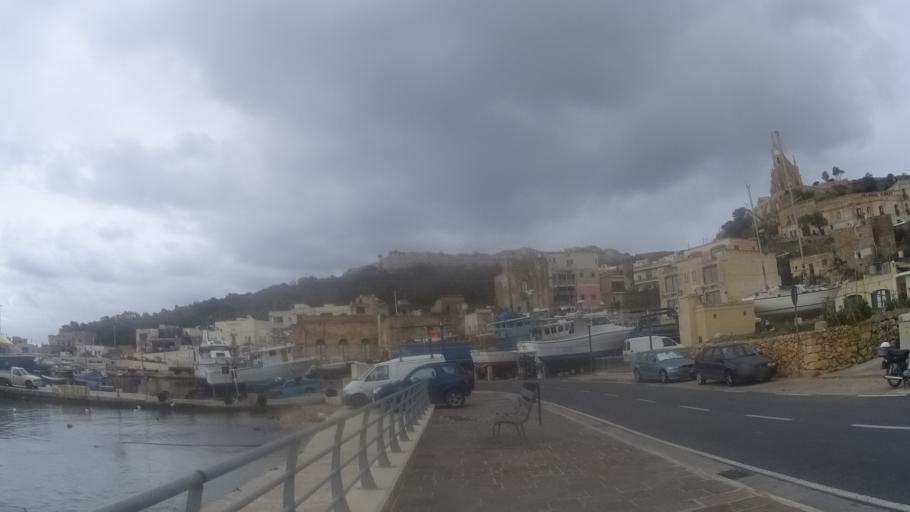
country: MT
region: Ghajnsielem
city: Mgarr
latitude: 36.0257
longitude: 14.2970
